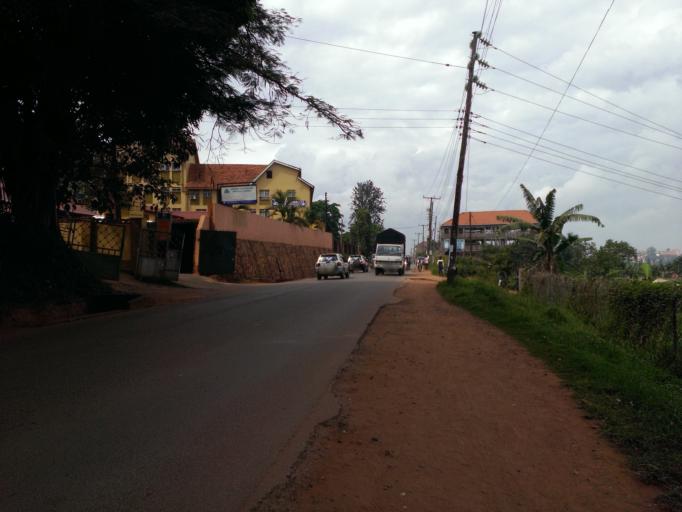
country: UG
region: Central Region
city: Kampala Central Division
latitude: 0.3156
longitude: 32.5575
